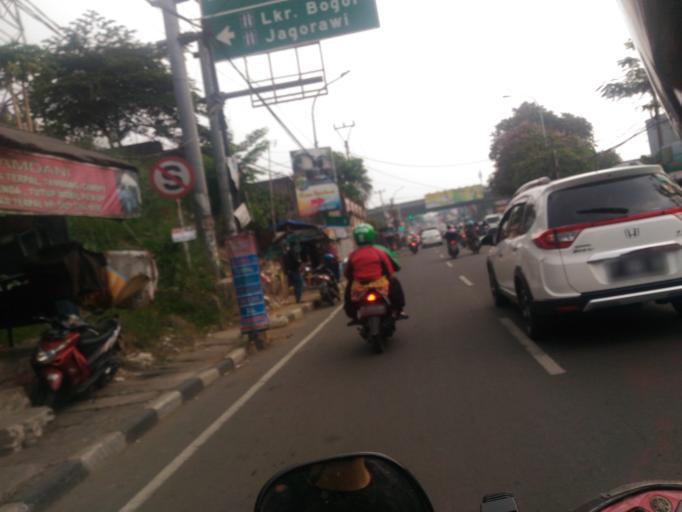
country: ID
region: West Java
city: Bogor
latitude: -6.5626
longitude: 106.8112
